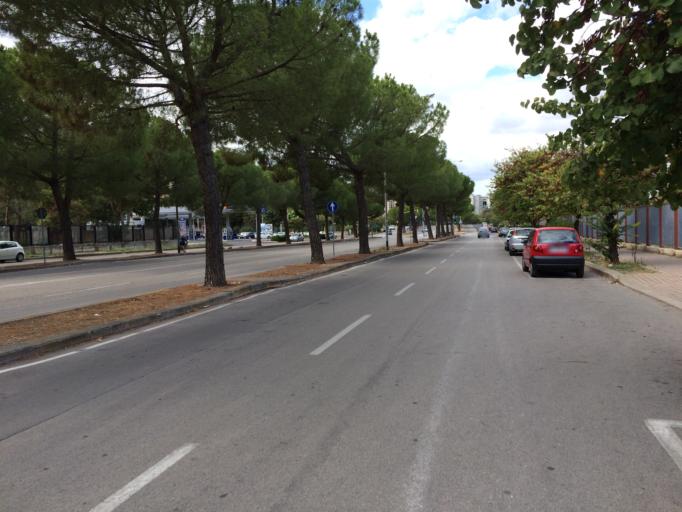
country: IT
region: Apulia
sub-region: Provincia di Bari
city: Bari
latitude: 41.0993
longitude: 16.8665
